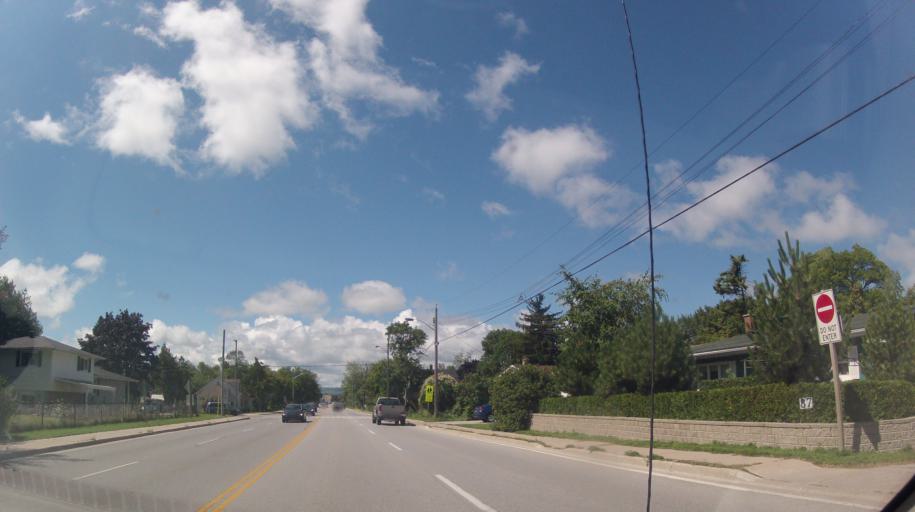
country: CA
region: Ontario
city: Collingwood
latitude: 44.5066
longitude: -80.2070
